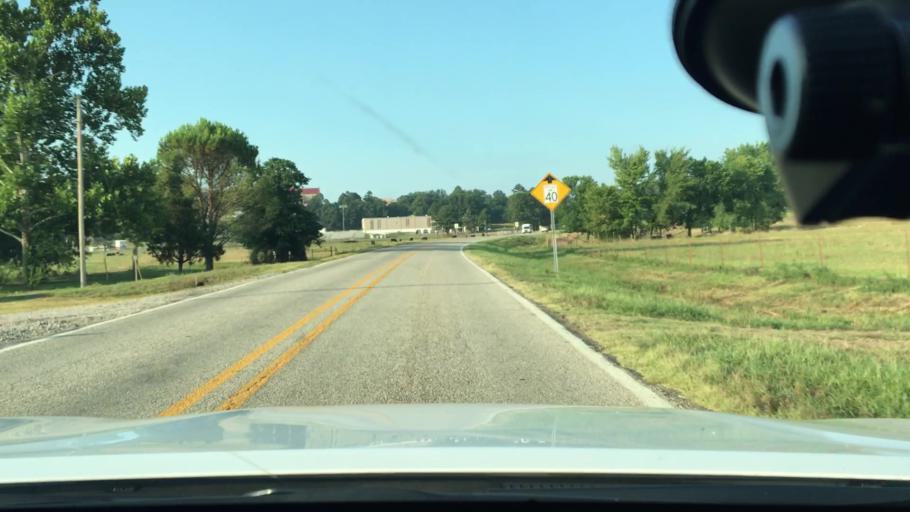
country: US
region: Arkansas
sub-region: Logan County
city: Paris
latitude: 35.3058
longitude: -93.6332
